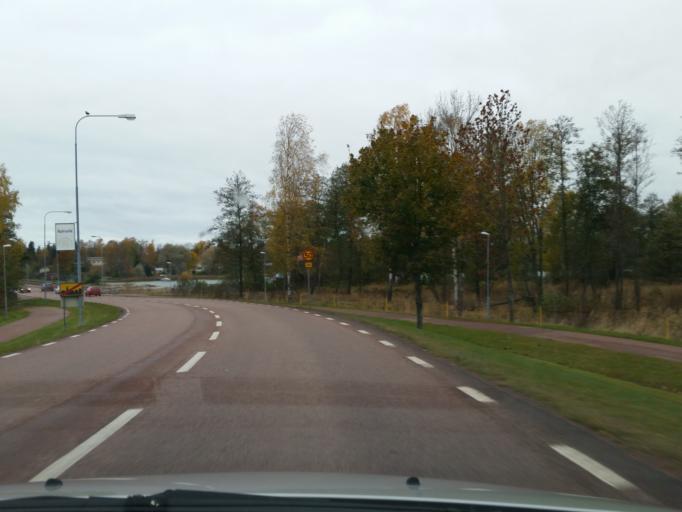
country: AX
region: Mariehamns stad
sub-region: Mariehamn
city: Mariehamn
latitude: 60.1143
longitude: 19.9267
